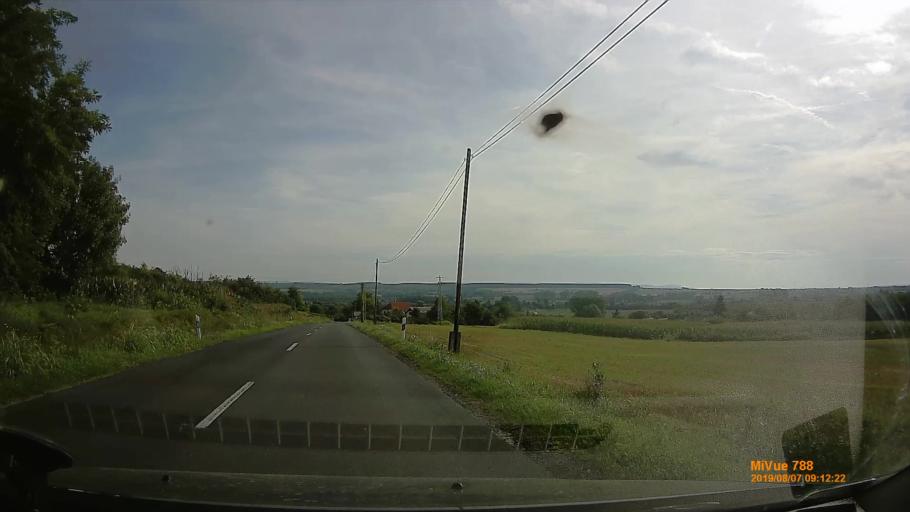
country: HU
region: Zala
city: Sarmellek
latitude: 46.7213
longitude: 17.1027
